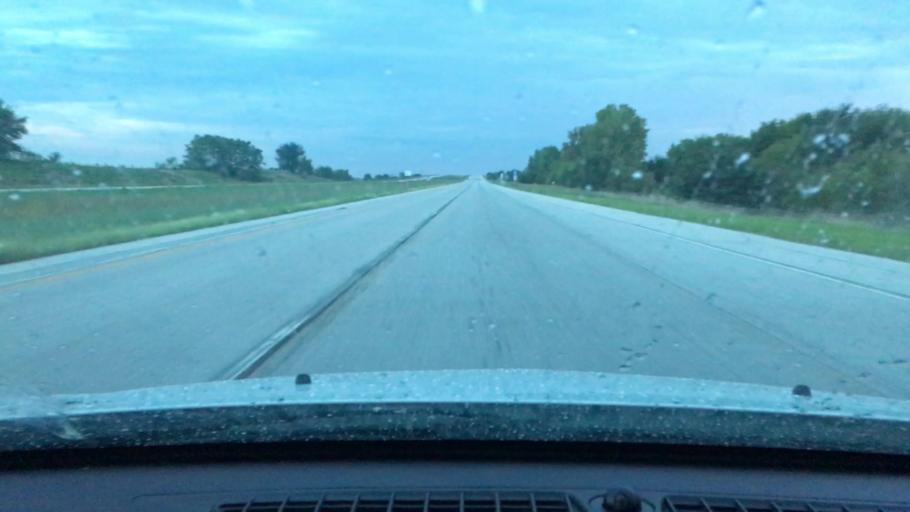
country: US
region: Illinois
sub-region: Morgan County
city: South Jacksonville
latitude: 39.7187
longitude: -90.1726
